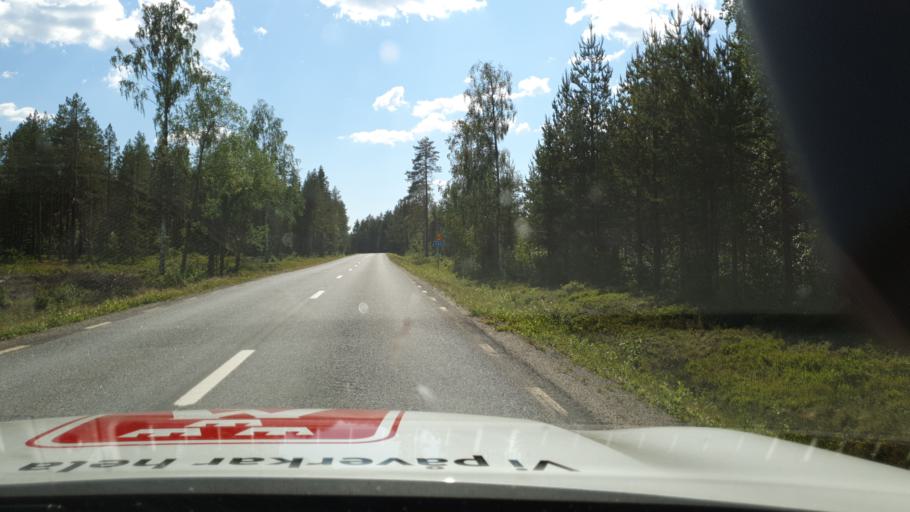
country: SE
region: Vaesterbotten
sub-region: Skelleftea Kommun
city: Burtraesk
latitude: 64.4084
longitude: 20.3920
